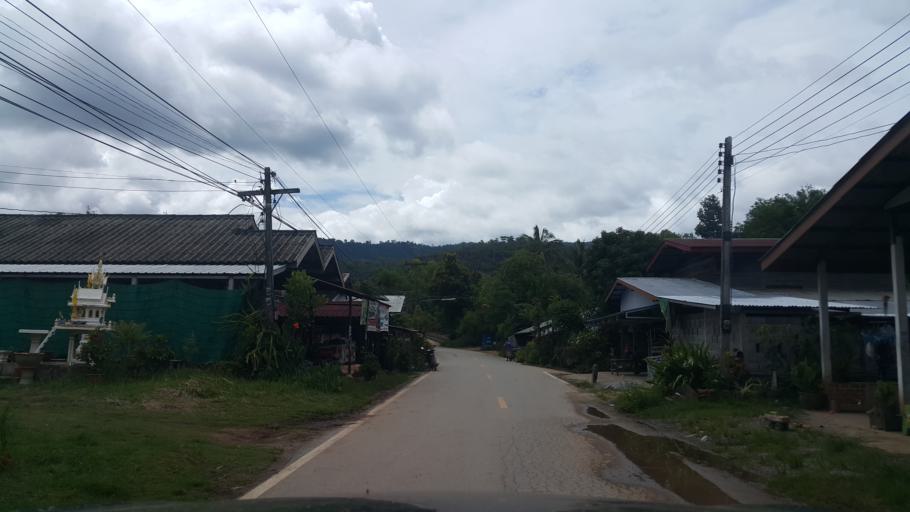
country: TH
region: Phitsanulok
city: Chat Trakan
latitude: 17.3035
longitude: 100.6701
